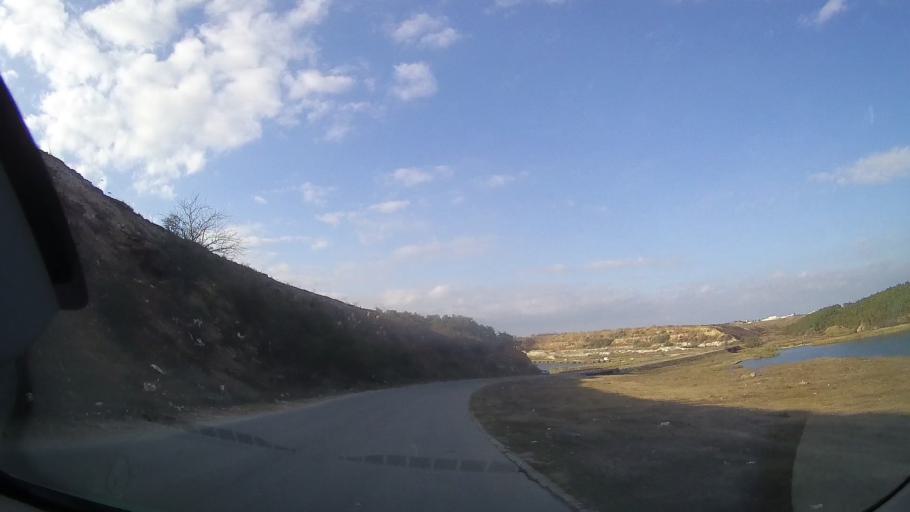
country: RO
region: Constanta
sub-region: Comuna Limanu
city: Limanu
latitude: 43.8107
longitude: 28.5178
